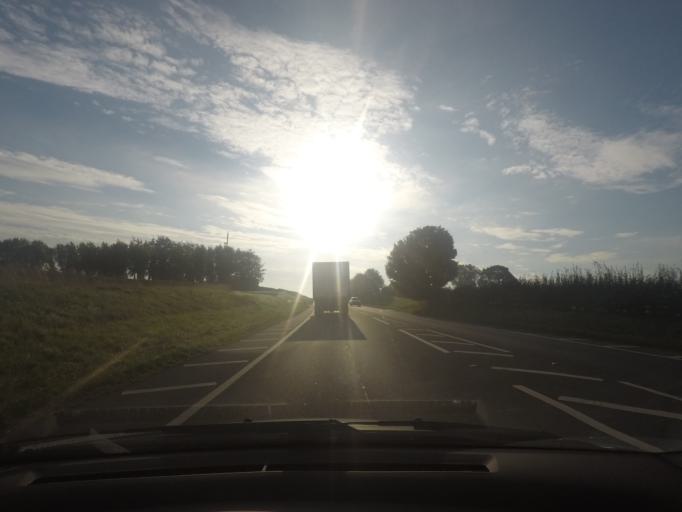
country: GB
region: England
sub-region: East Riding of Yorkshire
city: Hayton
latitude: 53.8852
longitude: -0.7251
